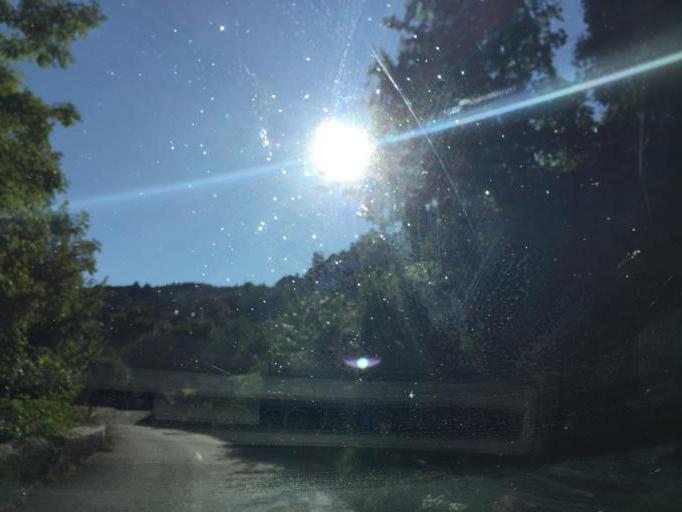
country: FR
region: Rhone-Alpes
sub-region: Departement de la Loire
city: Saint-Paul-en-Jarez
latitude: 45.4279
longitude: 4.5829
